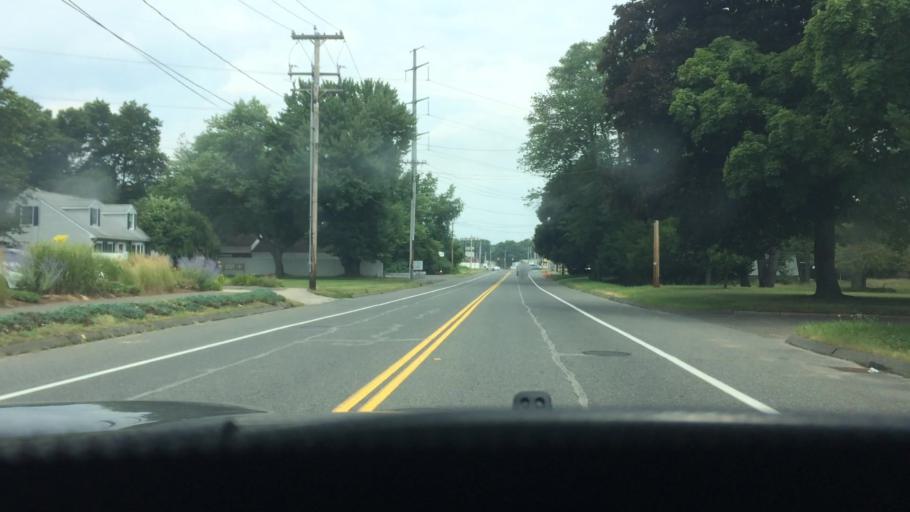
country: US
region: Massachusetts
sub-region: Hampden County
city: North Chicopee
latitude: 42.1703
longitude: -72.5861
